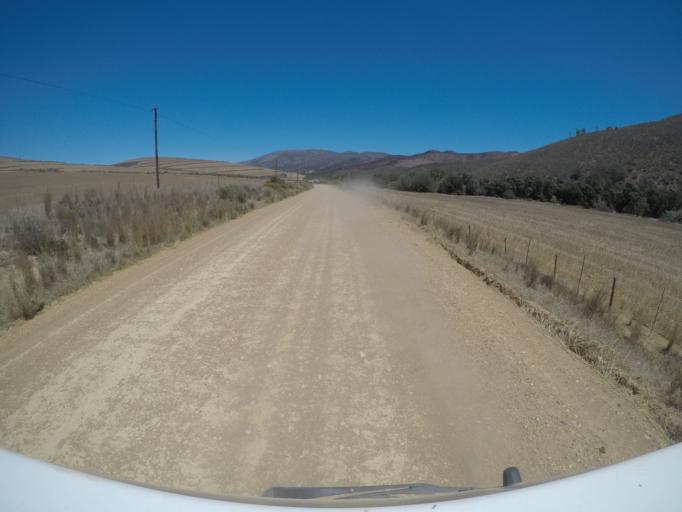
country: ZA
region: Western Cape
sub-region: Overberg District Municipality
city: Caledon
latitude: -34.1485
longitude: 19.2419
